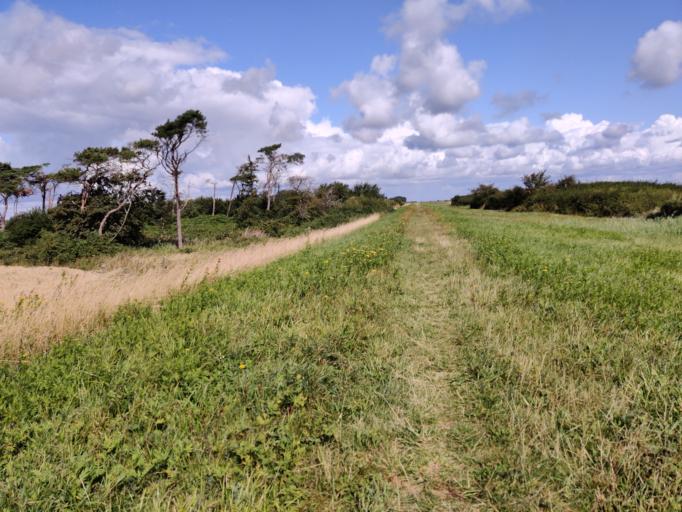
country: DK
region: Zealand
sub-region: Guldborgsund Kommune
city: Nykobing Falster
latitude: 54.5765
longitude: 11.9725
